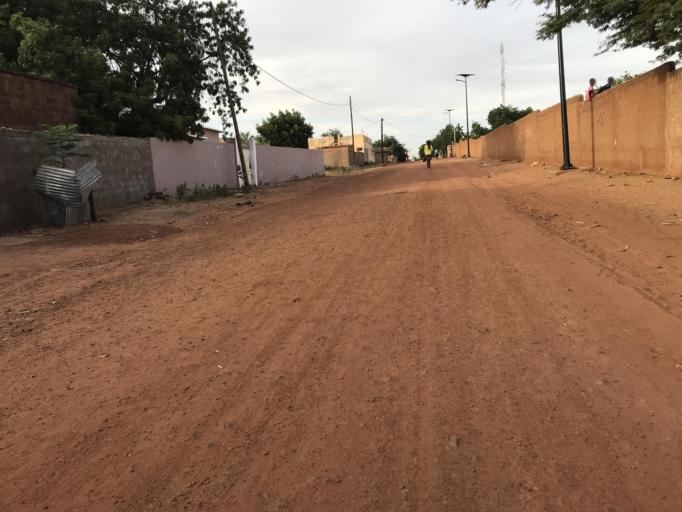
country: SN
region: Louga
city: Ndibene Dahra
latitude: 15.3988
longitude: -15.1165
